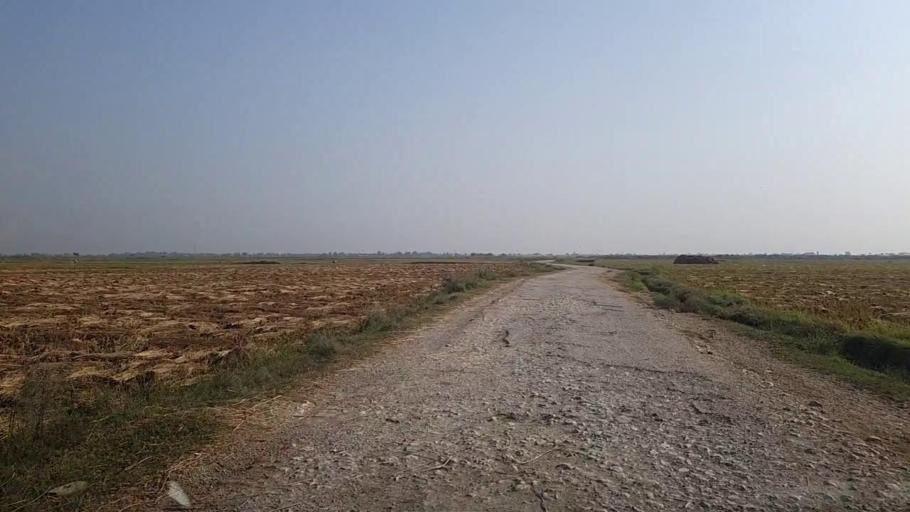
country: PK
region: Sindh
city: Kandhkot
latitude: 28.2996
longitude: 69.2516
